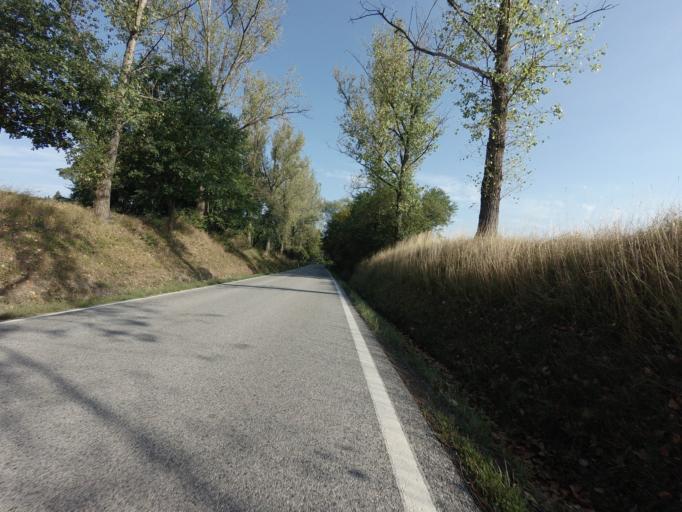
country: CZ
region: Jihocesky
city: Tyn nad Vltavou
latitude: 49.2381
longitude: 14.4204
